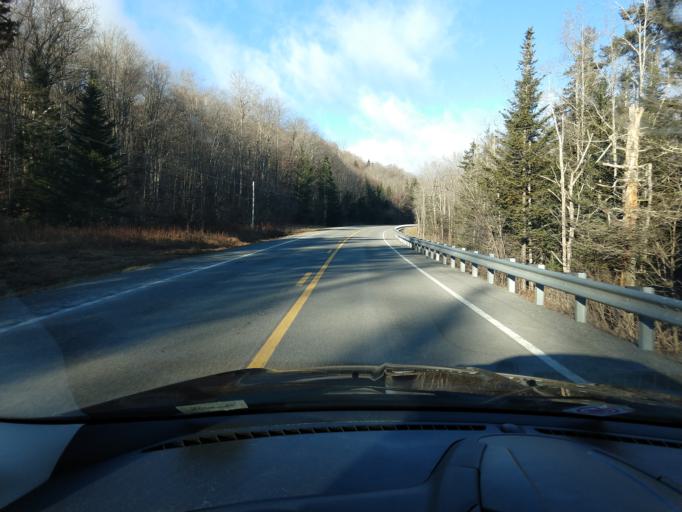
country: US
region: West Virginia
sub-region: Randolph County
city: Elkins
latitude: 38.6013
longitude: -79.8550
